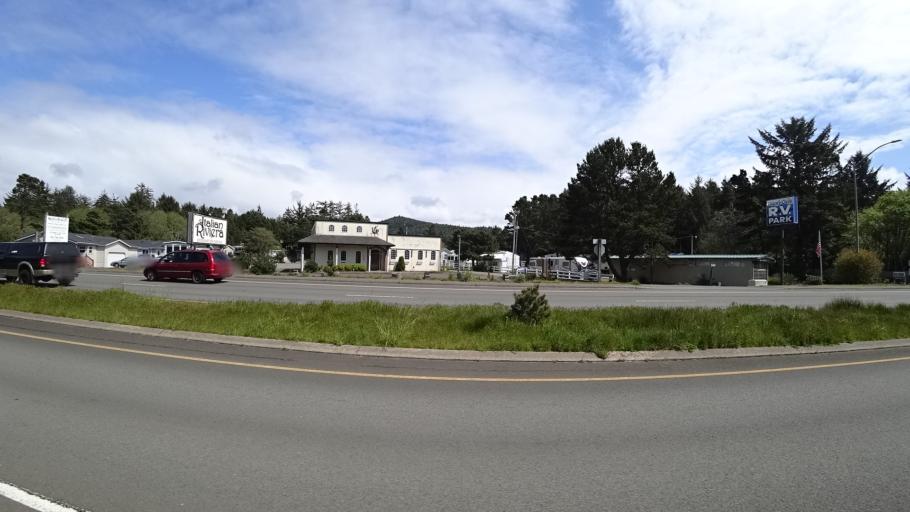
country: US
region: Oregon
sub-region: Lincoln County
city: Lincoln Beach
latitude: 44.8442
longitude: -124.0475
